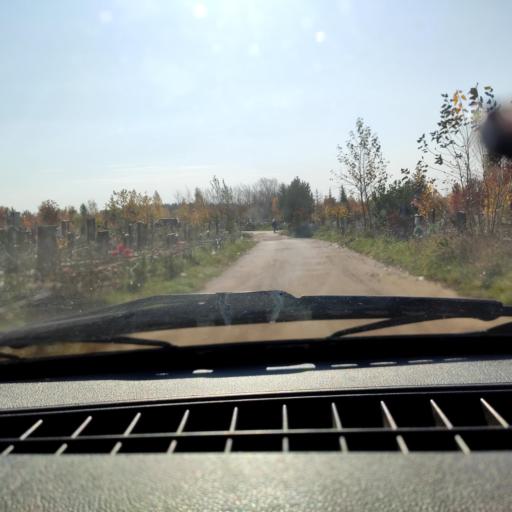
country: RU
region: Bashkortostan
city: Mikhaylovka
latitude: 54.8165
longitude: 55.8690
